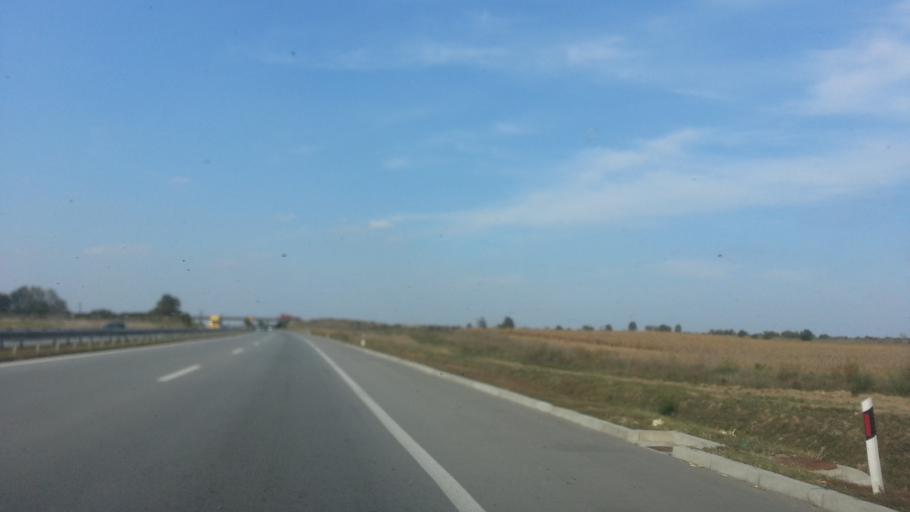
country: RS
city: Novi Banovci
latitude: 44.9121
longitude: 20.3055
